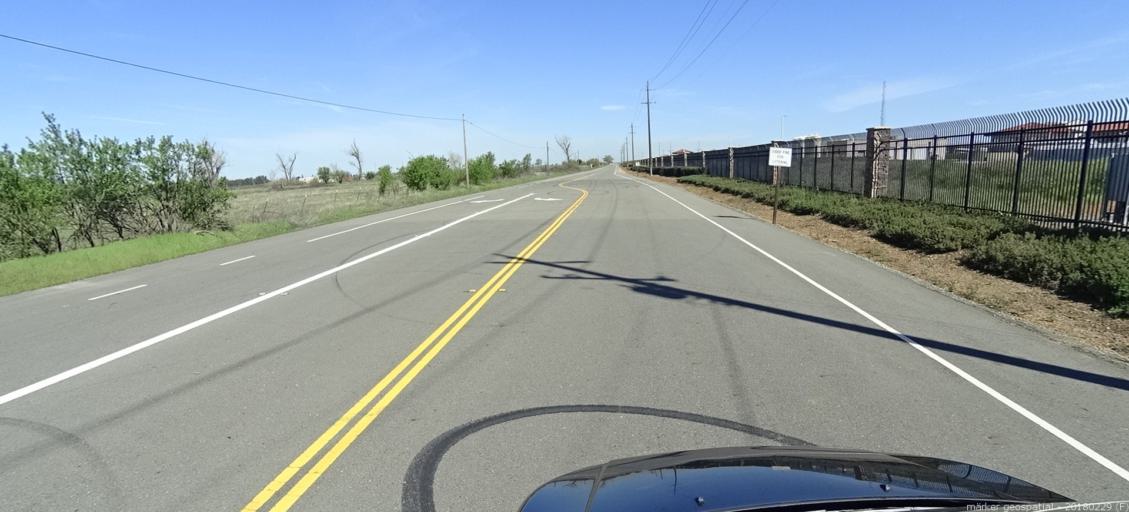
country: US
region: California
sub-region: Sacramento County
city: Vineyard
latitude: 38.4966
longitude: -121.3162
